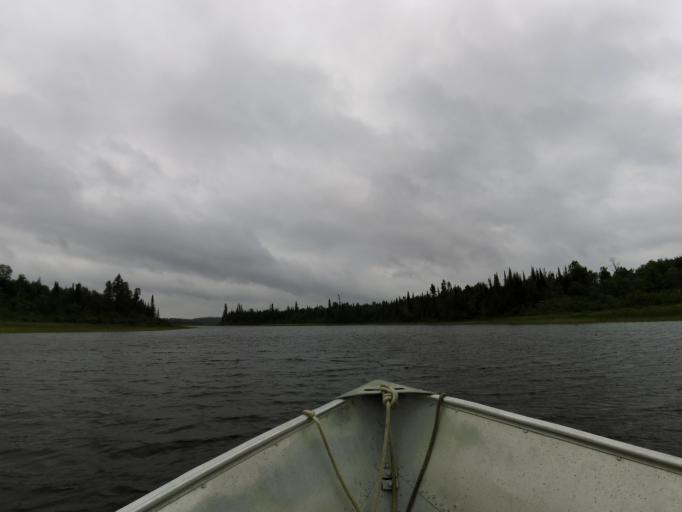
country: CA
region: Ontario
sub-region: Rainy River District
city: Atikokan
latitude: 49.5965
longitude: -91.3406
